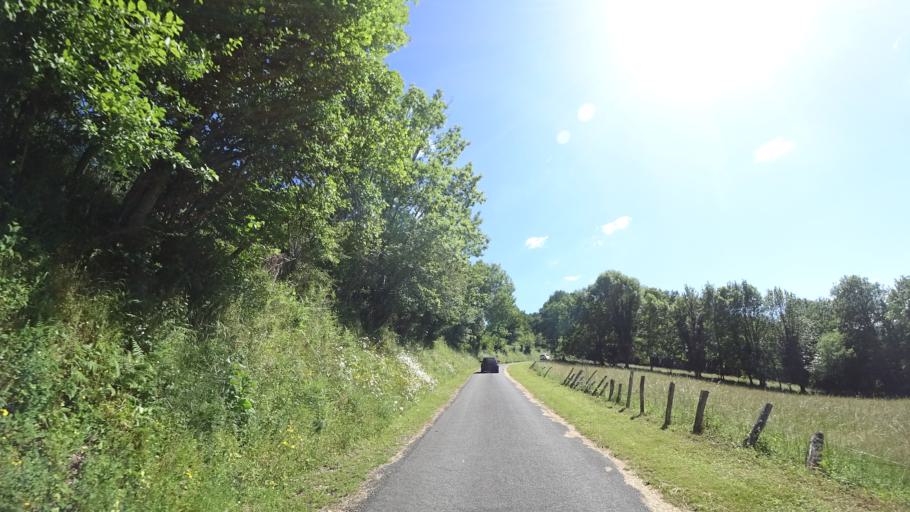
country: FR
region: Midi-Pyrenees
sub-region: Departement de l'Aveyron
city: Colombies
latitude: 44.3863
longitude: 2.3351
